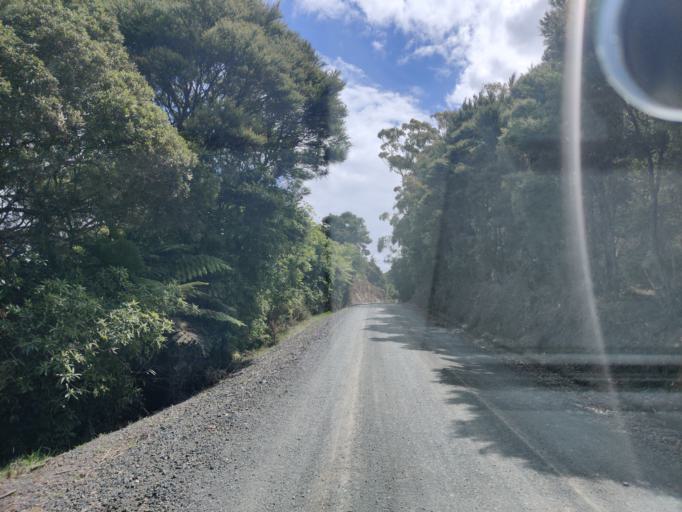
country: NZ
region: Northland
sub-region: Far North District
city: Paihia
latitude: -35.2595
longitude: 174.0596
